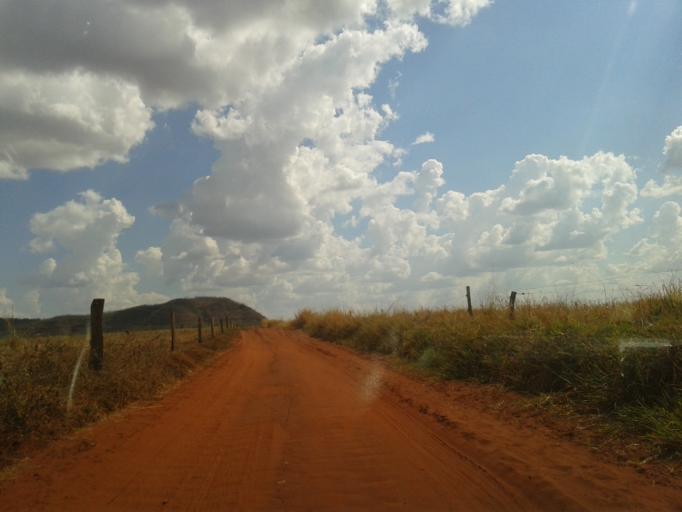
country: BR
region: Minas Gerais
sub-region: Santa Vitoria
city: Santa Vitoria
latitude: -19.1972
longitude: -49.9257
